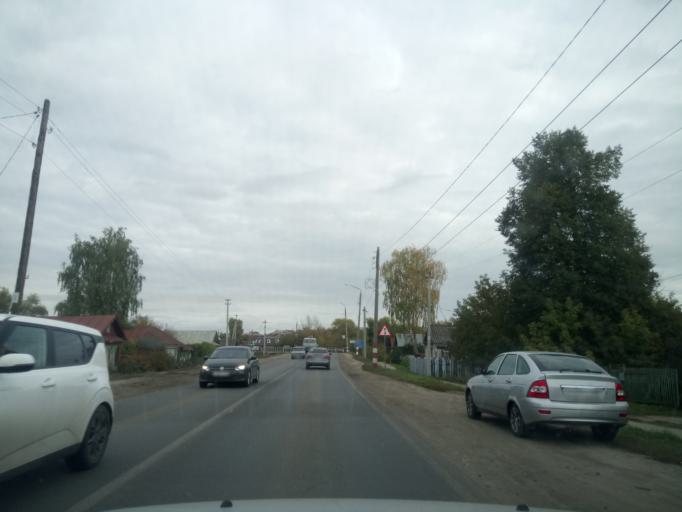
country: RU
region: Nizjnij Novgorod
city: Lukoyanov
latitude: 55.0301
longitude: 44.4883
